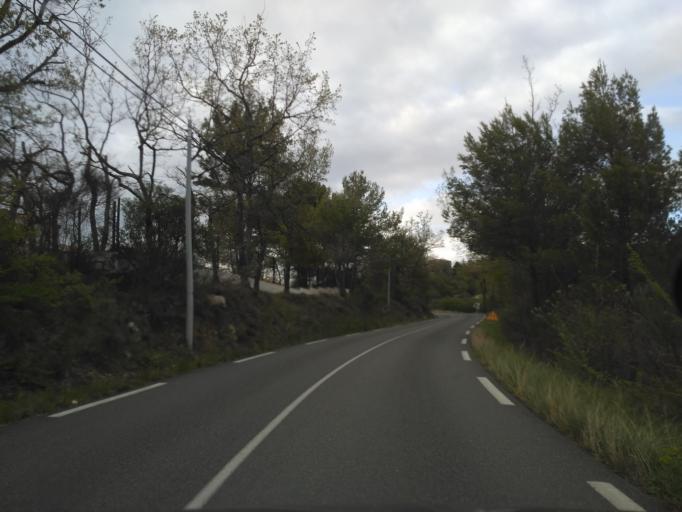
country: FR
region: Provence-Alpes-Cote d'Azur
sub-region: Departement du Var
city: Saint-Julien
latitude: 43.6267
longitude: 5.9428
